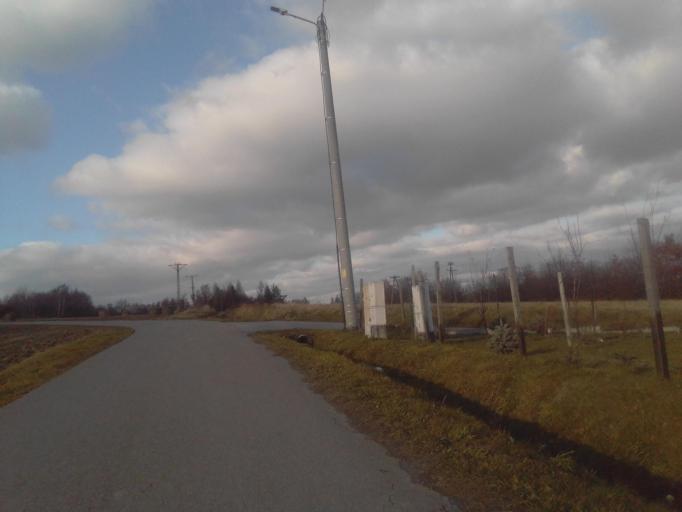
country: PL
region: Subcarpathian Voivodeship
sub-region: Powiat strzyzowski
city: Babica
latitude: 49.9393
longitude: 21.8966
